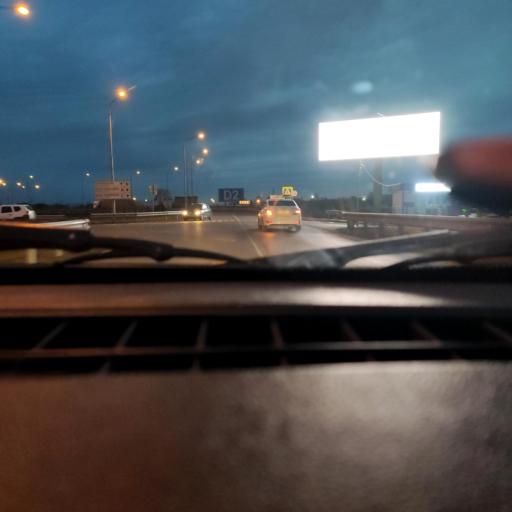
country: RU
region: Bashkortostan
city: Ufa
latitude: 54.5688
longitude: 55.8892
